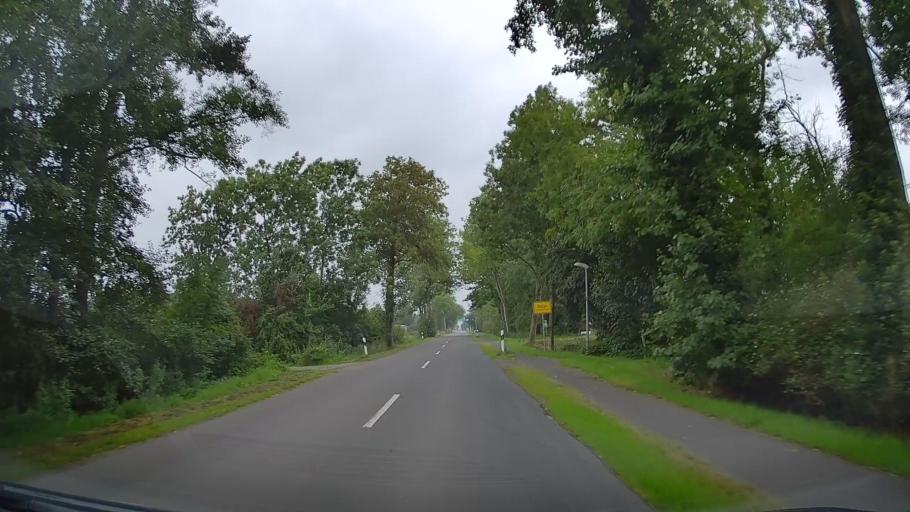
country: DE
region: Lower Saxony
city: Balje
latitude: 53.8244
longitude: 9.1324
